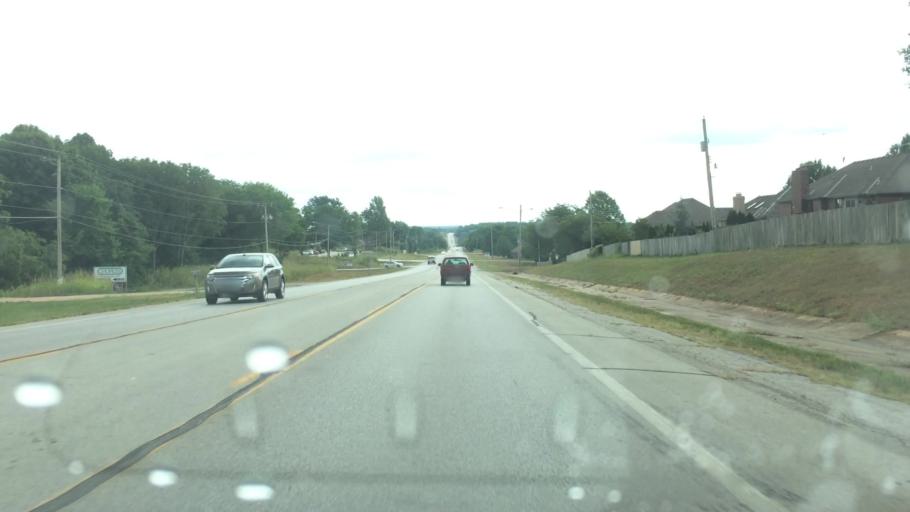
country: US
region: Missouri
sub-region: Greene County
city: Springfield
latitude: 37.1799
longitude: -93.2145
